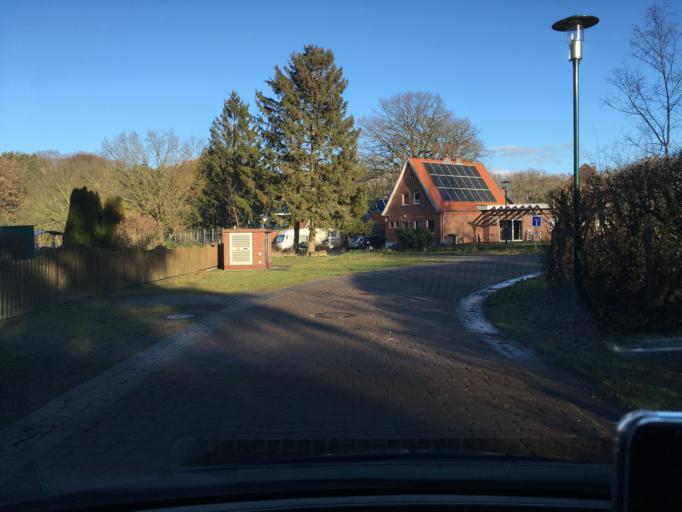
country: DE
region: Lower Saxony
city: Wendisch Evern
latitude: 53.2164
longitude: 10.4736
